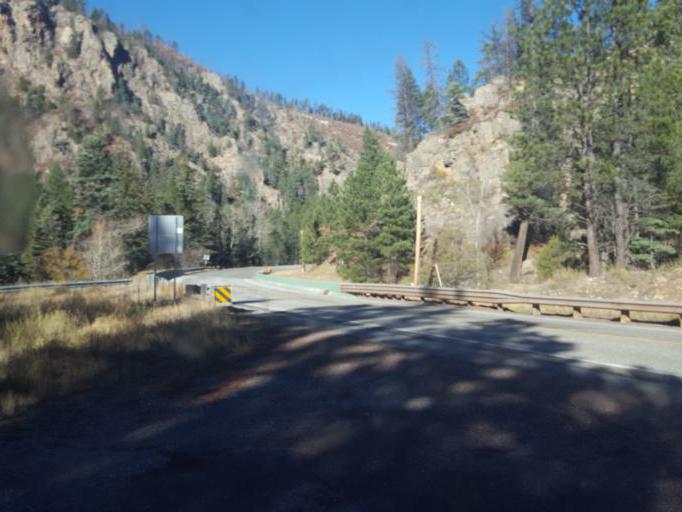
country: US
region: New Mexico
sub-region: Taos County
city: Ranchos de Taos
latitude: 36.1581
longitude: -105.5925
